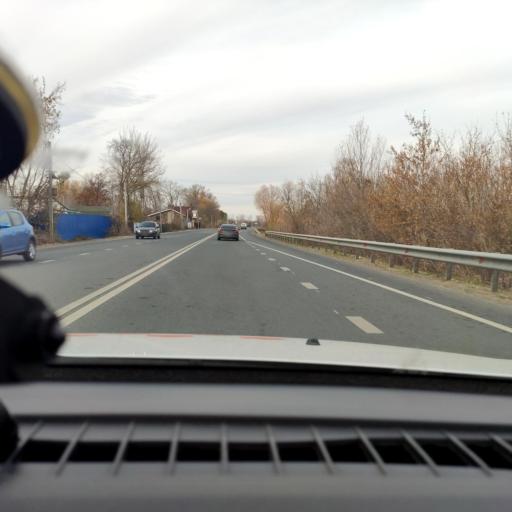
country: RU
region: Samara
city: Novokuybyshevsk
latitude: 53.1442
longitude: 49.9963
